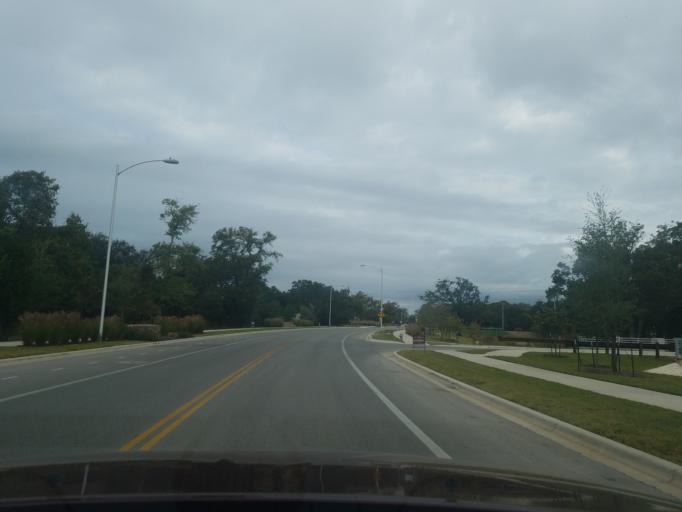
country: US
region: Texas
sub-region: Williamson County
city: Anderson Mill
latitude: 30.4761
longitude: -97.7858
